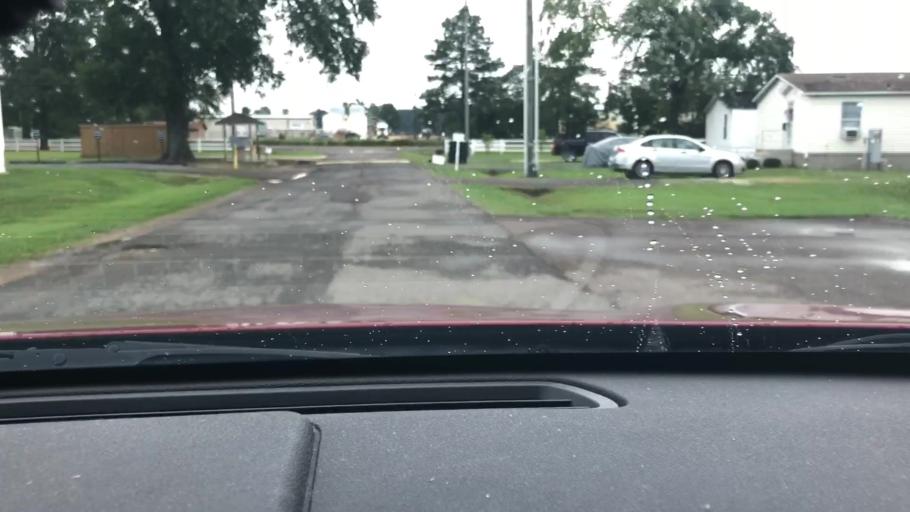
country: US
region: Texas
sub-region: Bowie County
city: Nash
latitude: 33.4429
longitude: -94.1382
